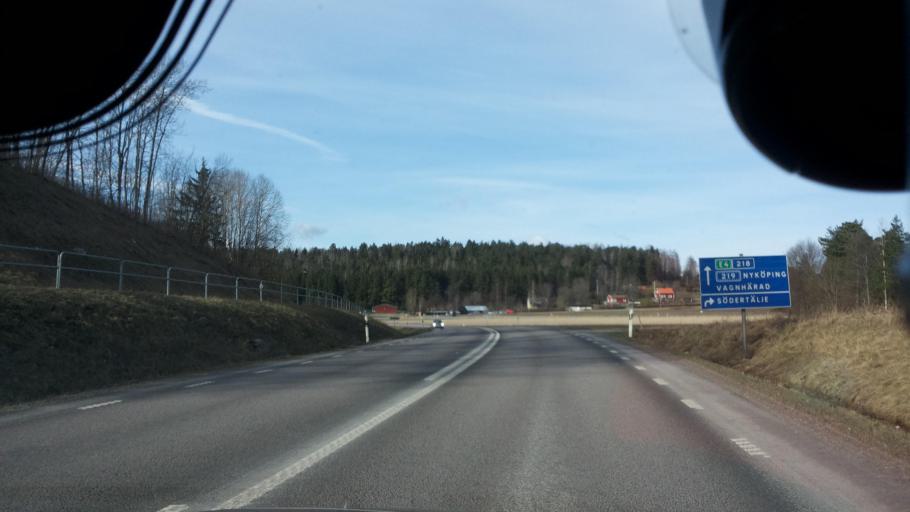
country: SE
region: Soedermanland
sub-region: Trosa Kommun
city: Vagnharad
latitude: 58.9427
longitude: 17.5195
